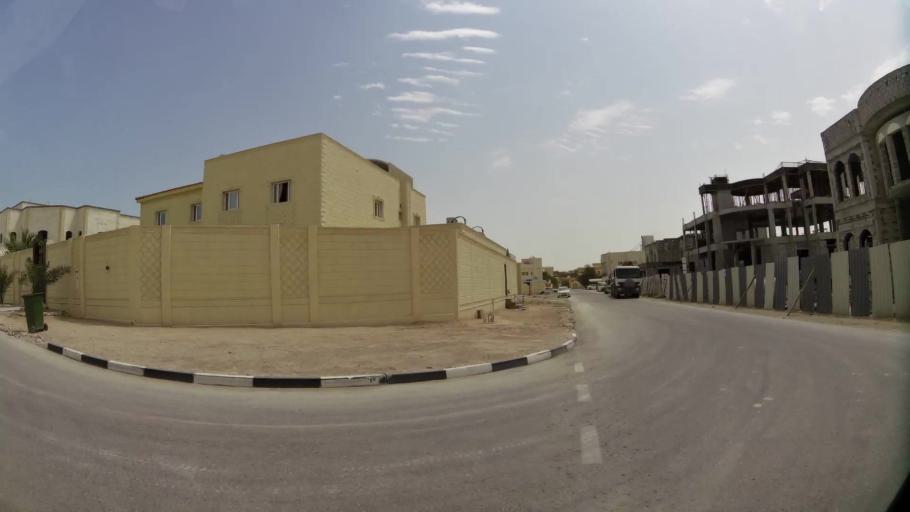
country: QA
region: Baladiyat ar Rayyan
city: Ar Rayyan
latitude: 25.3557
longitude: 51.4716
